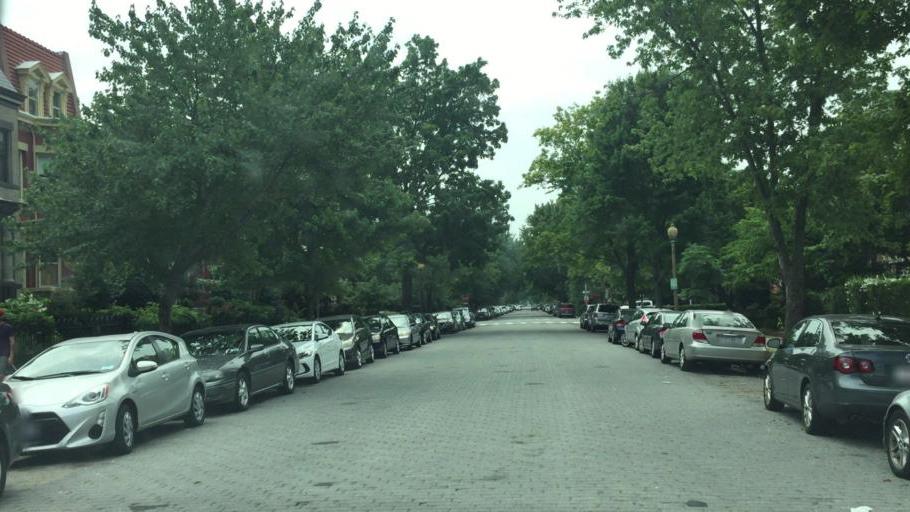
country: US
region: Washington, D.C.
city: Washington, D.C.
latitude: 38.8884
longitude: -76.9903
